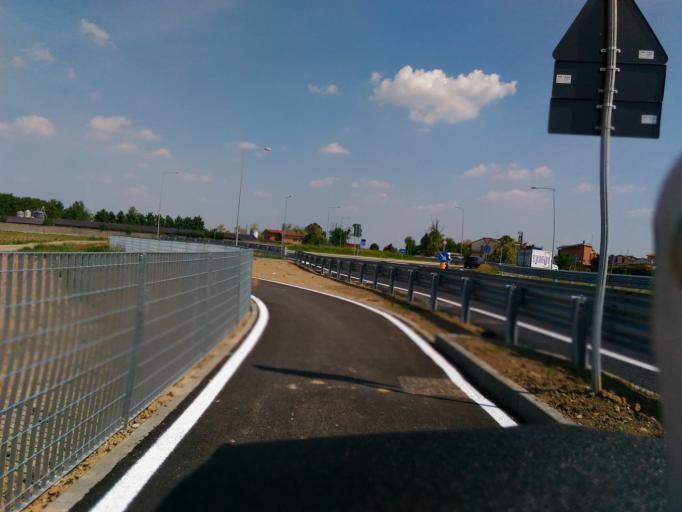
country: IT
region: Lombardy
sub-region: Citta metropolitana di Milano
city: Dresano
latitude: 45.3785
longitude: 9.3583
